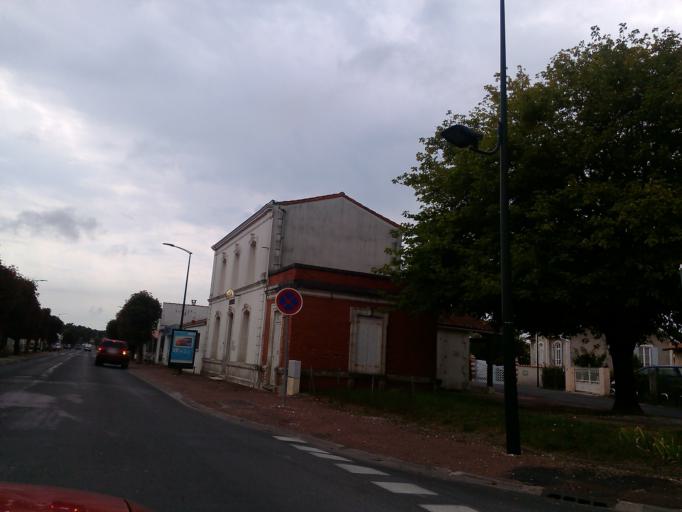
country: FR
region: Poitou-Charentes
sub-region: Departement de la Charente-Maritime
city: La Tremblade
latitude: 45.7643
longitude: -1.1423
